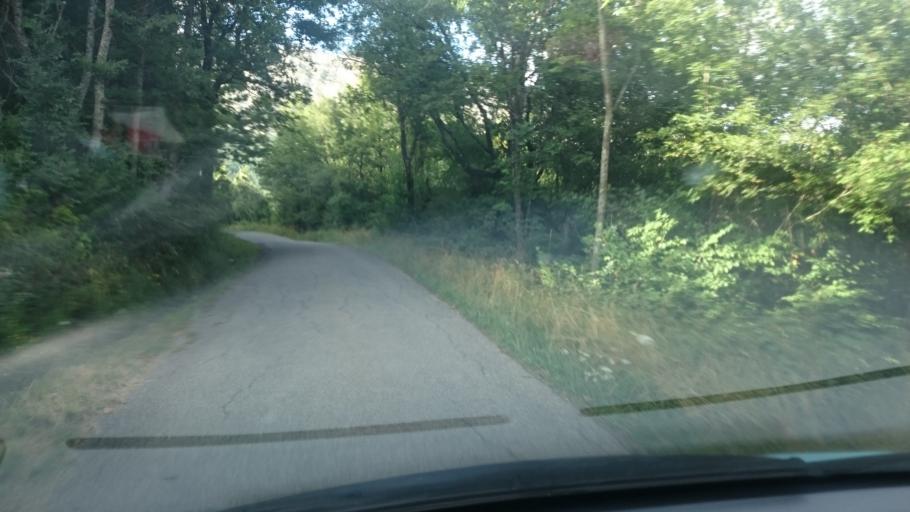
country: IT
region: Emilia-Romagna
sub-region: Provincia di Reggio Emilia
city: Villa Minozzo
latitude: 44.3063
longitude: 10.4488
